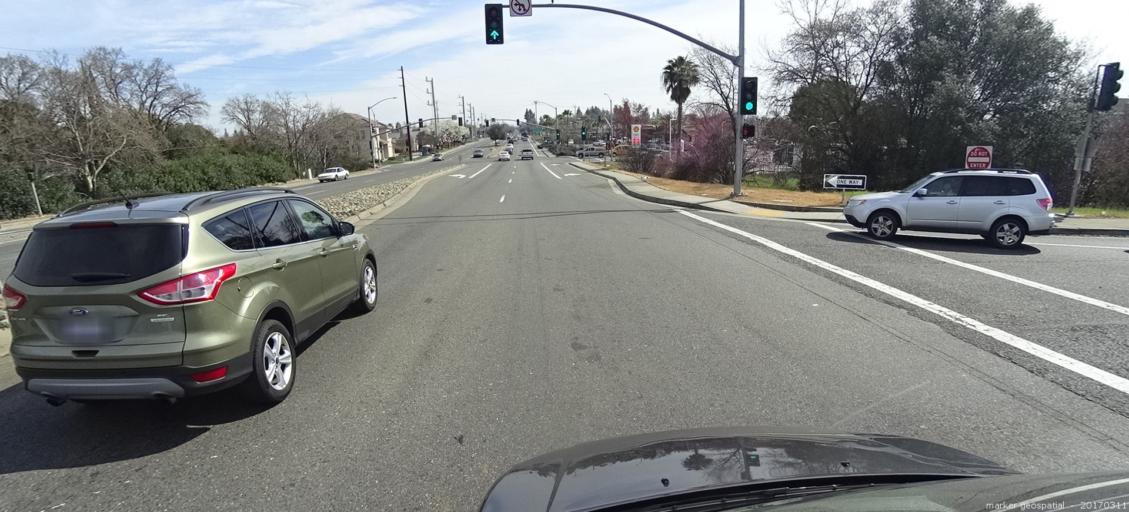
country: US
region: California
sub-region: Sacramento County
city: Parkway
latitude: 38.4812
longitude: -121.5088
